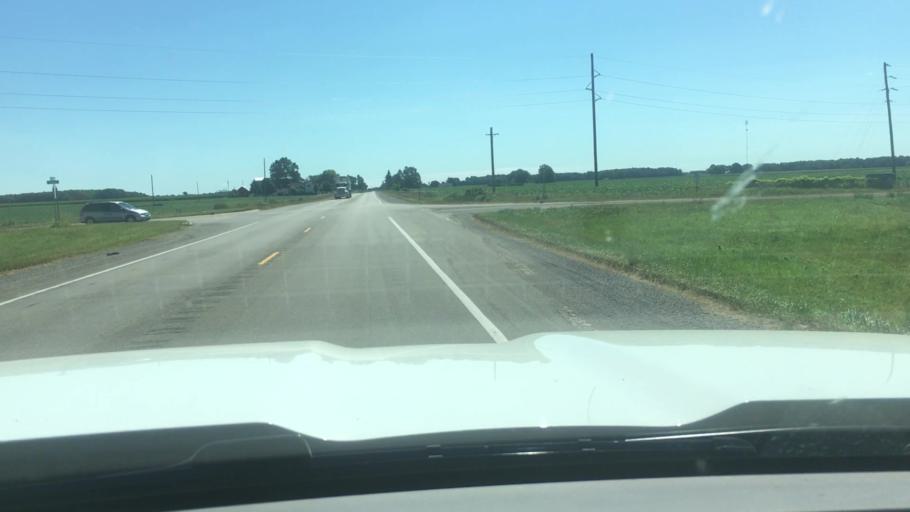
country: US
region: Michigan
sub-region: Montcalm County
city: Carson City
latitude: 43.1764
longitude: -84.7789
